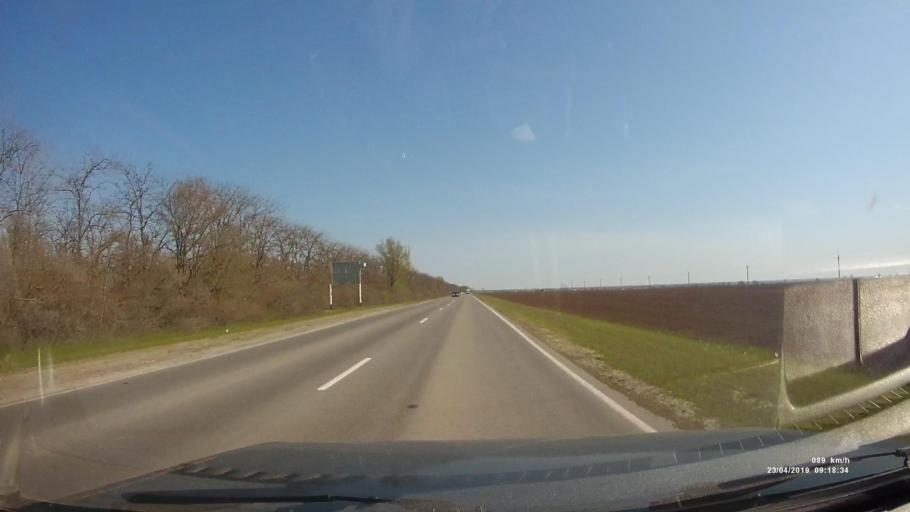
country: RU
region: Rostov
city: Proletarsk
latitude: 46.6659
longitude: 41.6896
